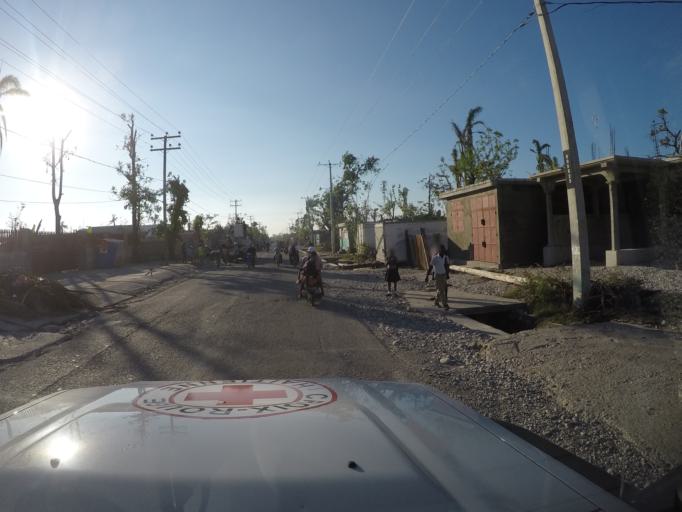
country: HT
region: Sud
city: Aquin
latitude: 18.3072
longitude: -73.3245
